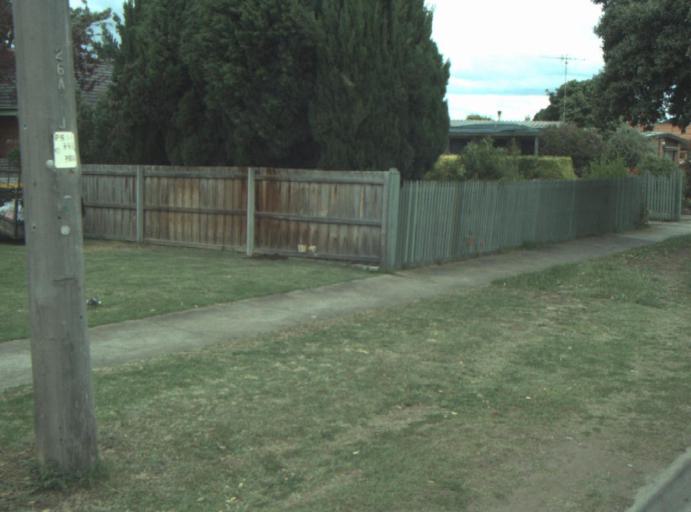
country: AU
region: Victoria
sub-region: Greater Geelong
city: Bell Park
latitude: -38.0736
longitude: 144.3662
